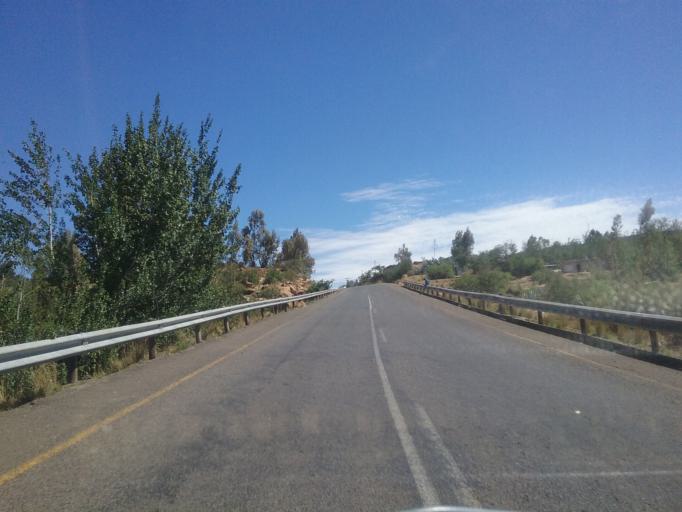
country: LS
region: Quthing
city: Quthing
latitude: -30.3657
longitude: 27.5506
